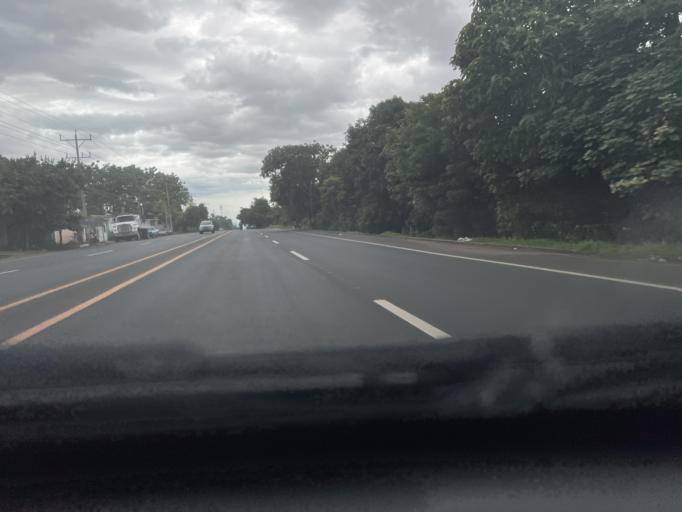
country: SV
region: Ahuachapan
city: Atiquizaya
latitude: 13.9725
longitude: -89.7179
